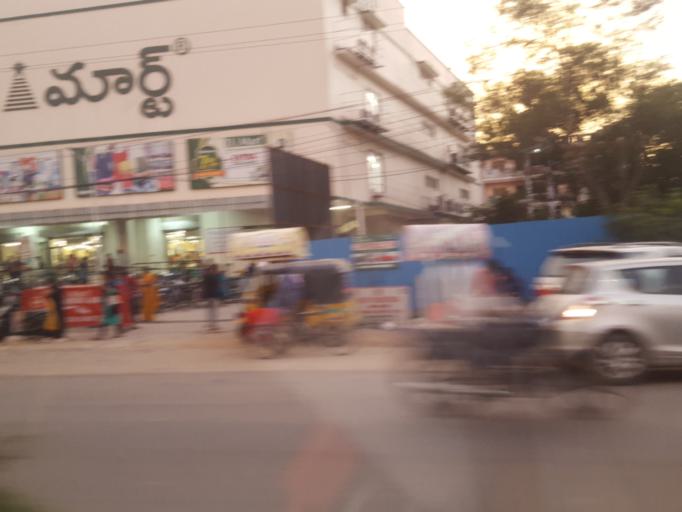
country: IN
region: Telangana
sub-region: Rangareddi
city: Kukatpalli
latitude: 17.5041
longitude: 78.3621
